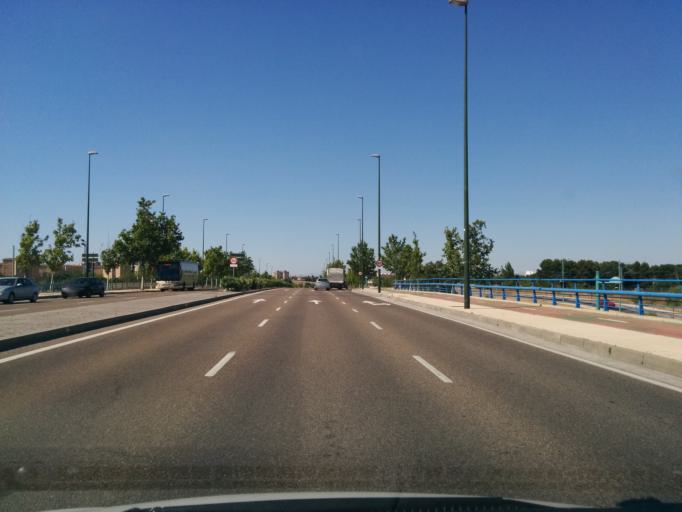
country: ES
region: Aragon
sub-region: Provincia de Zaragoza
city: Zaragoza
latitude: 41.6519
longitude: -0.8543
